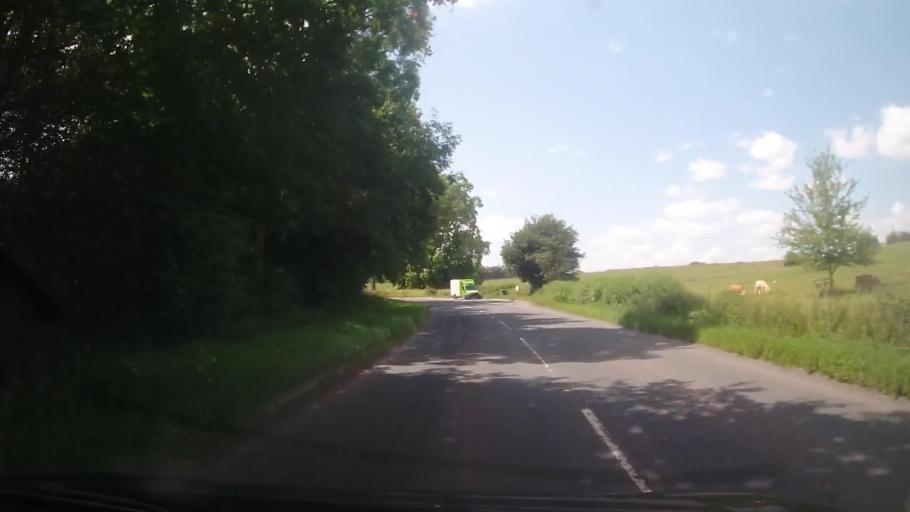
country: GB
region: England
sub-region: Herefordshire
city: Bodenham
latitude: 52.1704
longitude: -2.6961
